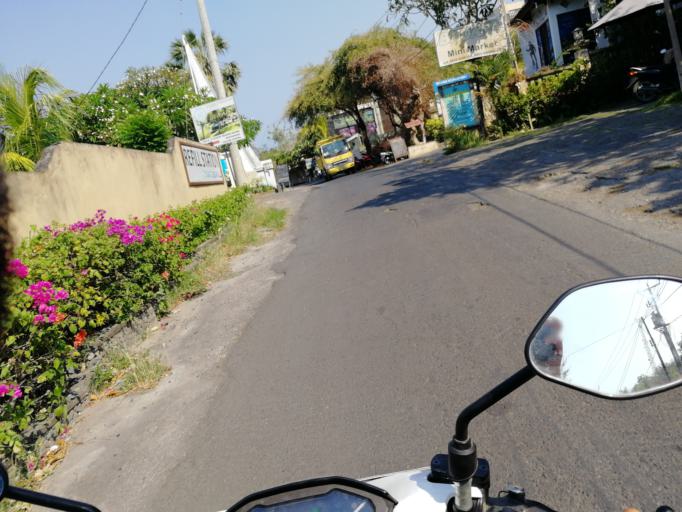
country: ID
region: Bali
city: Biaslantang Kaler
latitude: -8.3471
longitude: 115.6787
